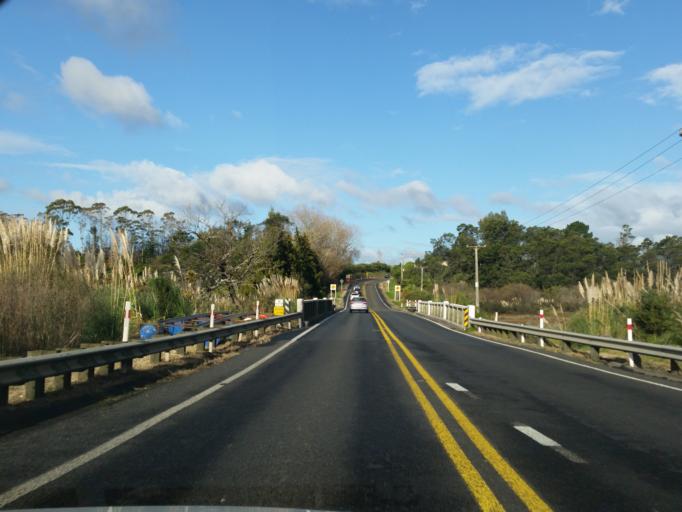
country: NZ
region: Bay of Plenty
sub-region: Western Bay of Plenty District
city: Katikati
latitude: -37.6338
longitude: 175.9592
